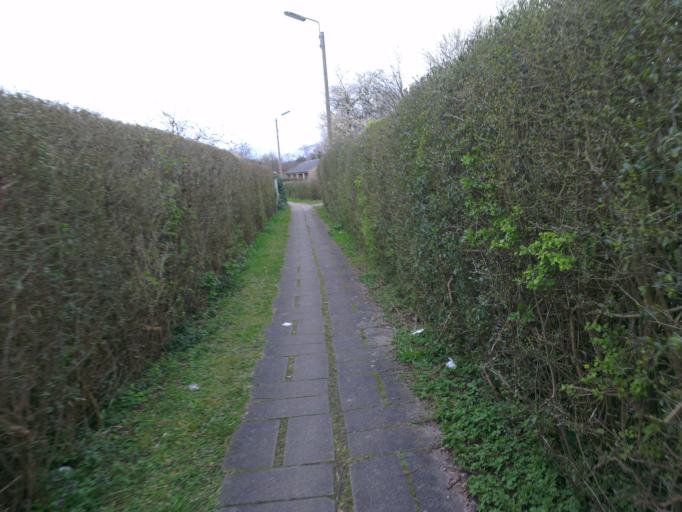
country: DK
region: Capital Region
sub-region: Frederikssund Kommune
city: Frederikssund
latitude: 55.8425
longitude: 12.0732
